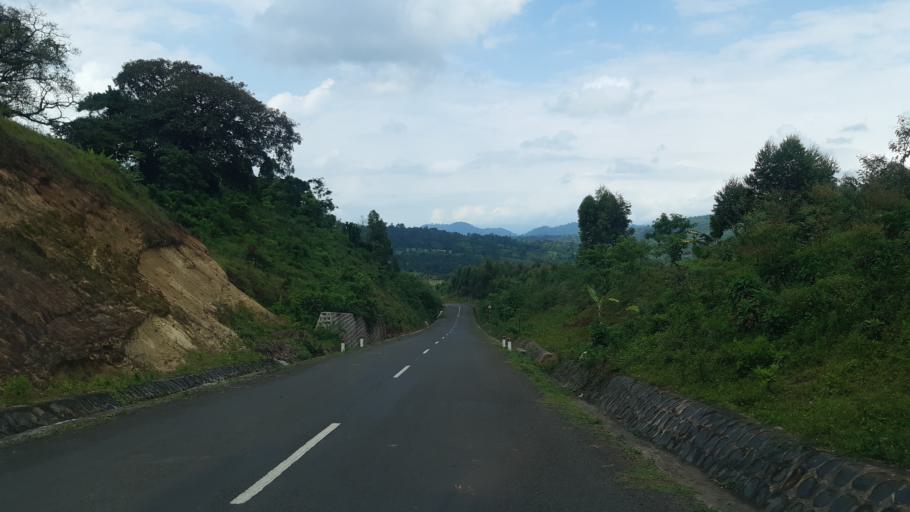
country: ET
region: Southern Nations, Nationalities, and People's Region
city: Bonga
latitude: 7.2254
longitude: 36.2676
